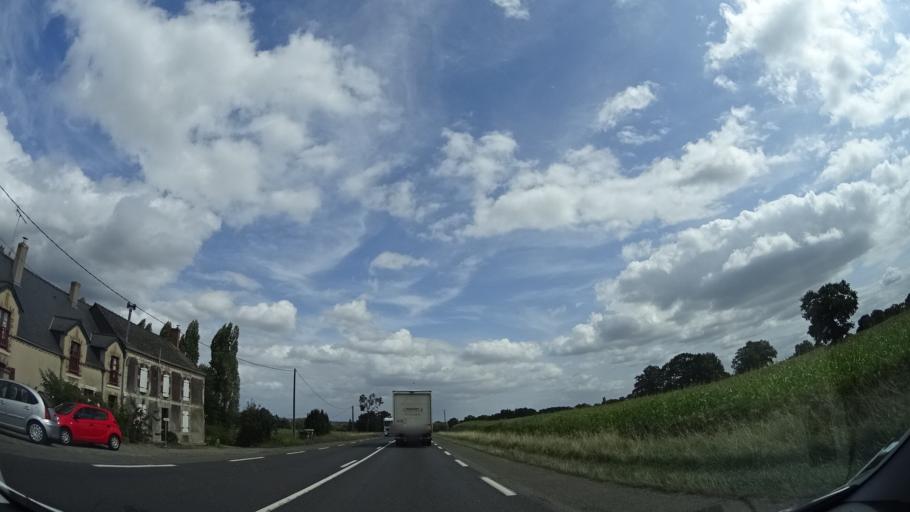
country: FR
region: Pays de la Loire
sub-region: Departement de la Mayenne
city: Saint-Berthevin
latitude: 48.0721
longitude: -0.8632
